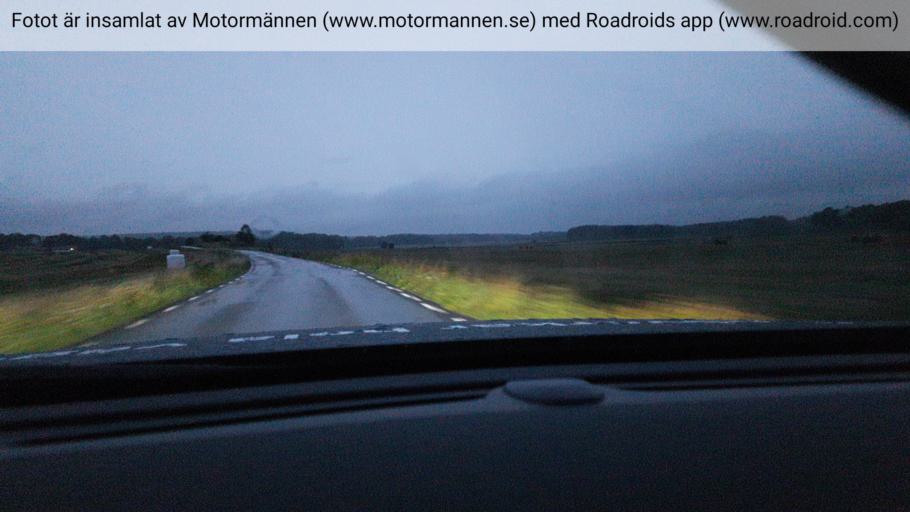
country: SE
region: Vaestra Goetaland
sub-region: Tidaholms Kommun
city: Tidaholm
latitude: 58.1730
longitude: 13.8189
